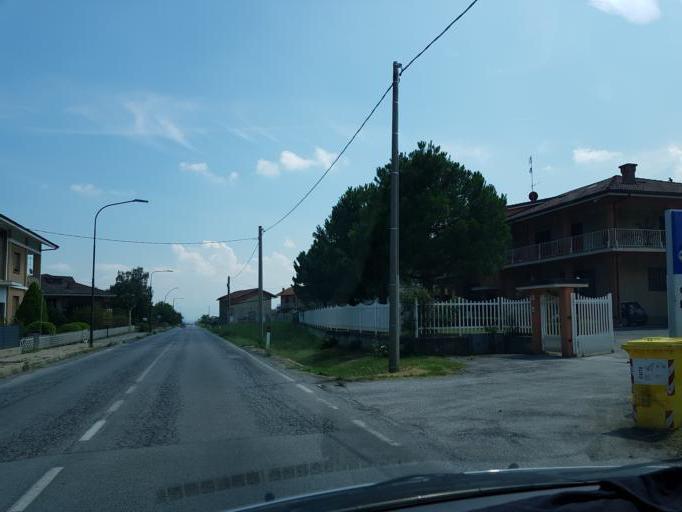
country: IT
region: Piedmont
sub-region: Provincia di Cuneo
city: Dronero
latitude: 44.4570
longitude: 7.3799
